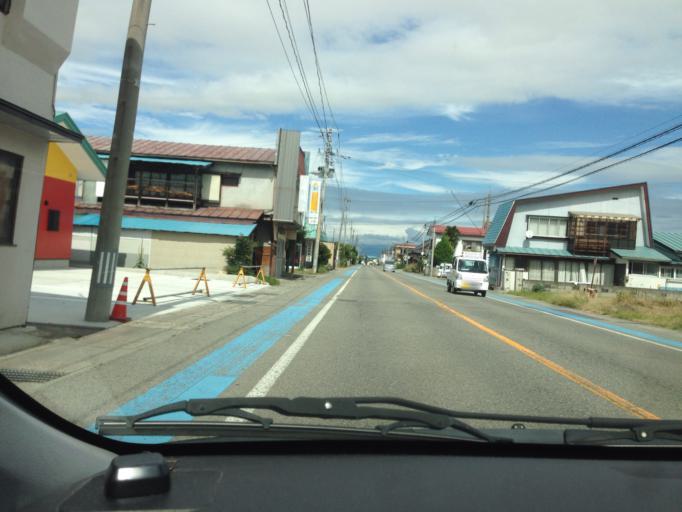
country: JP
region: Fukushima
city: Kitakata
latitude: 37.4653
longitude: 139.8447
